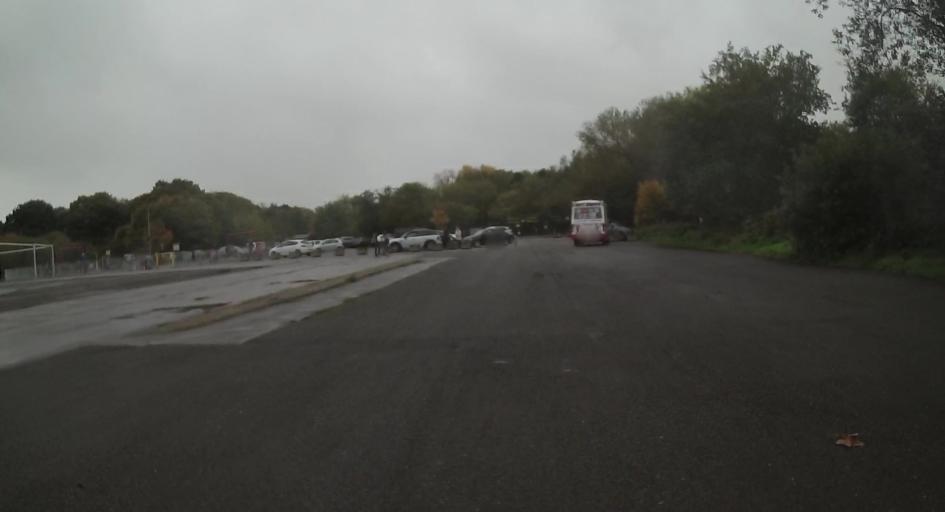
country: GB
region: England
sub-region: Surrey
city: Byfleet
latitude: 51.3444
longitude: -0.4717
